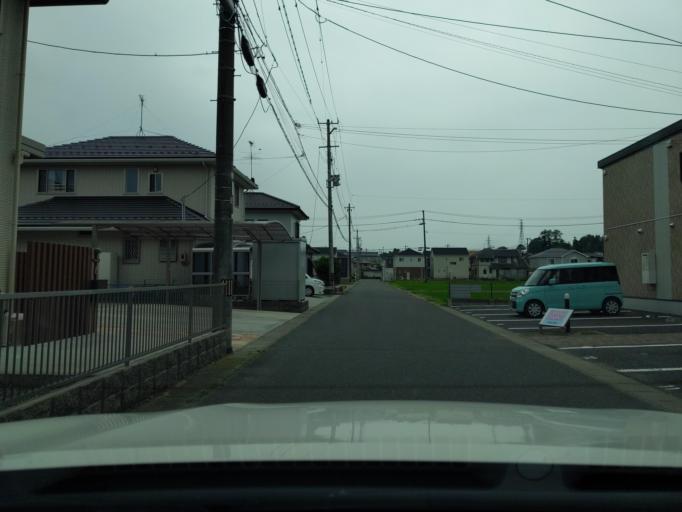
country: JP
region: Fukushima
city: Koriyama
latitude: 37.3556
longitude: 140.3590
